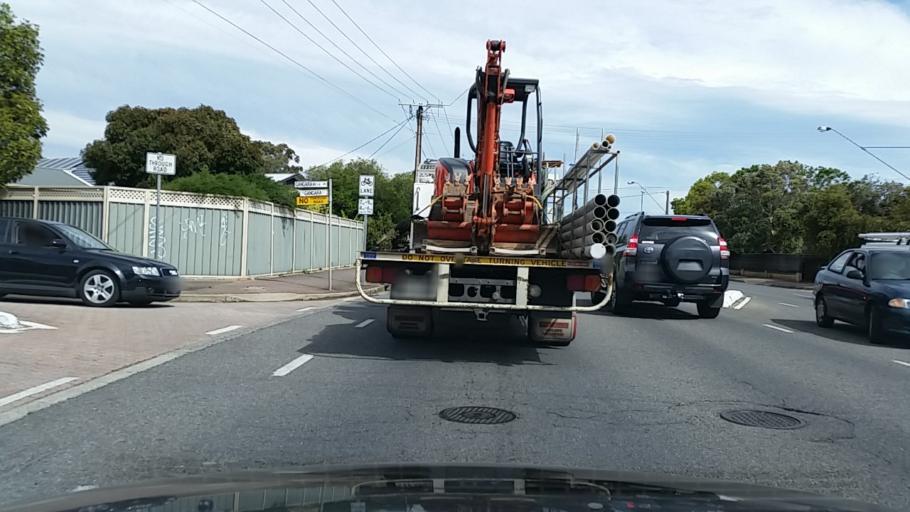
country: AU
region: South Australia
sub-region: Holdfast Bay
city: North Brighton
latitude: -35.0065
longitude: 138.5375
